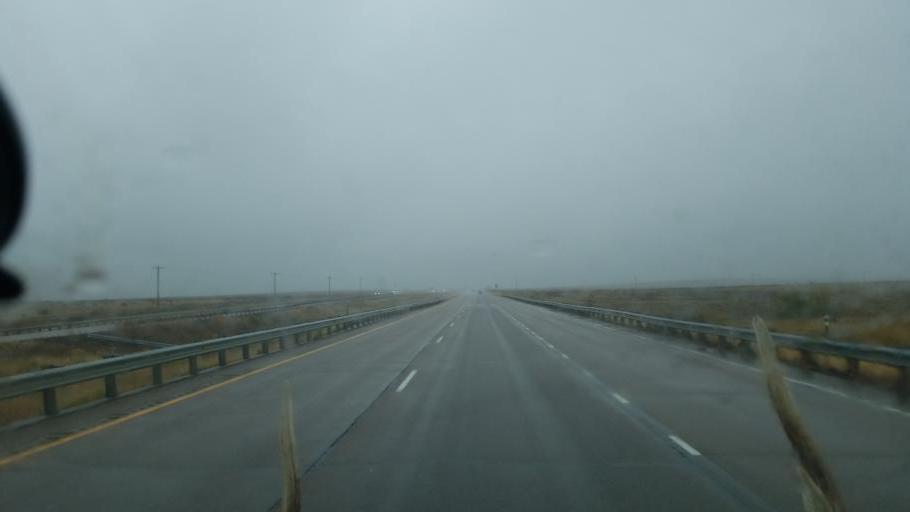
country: US
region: Colorado
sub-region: Pueblo County
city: Pueblo
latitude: 38.1322
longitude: -104.6673
